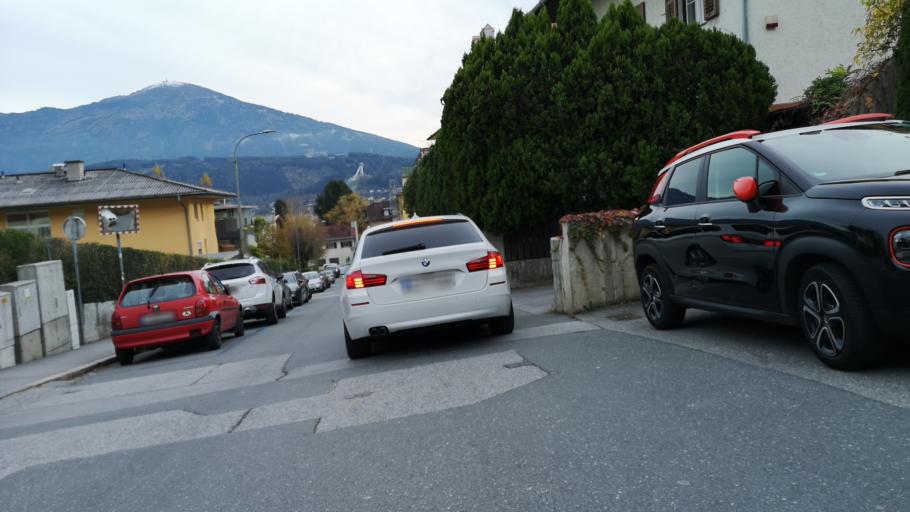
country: AT
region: Tyrol
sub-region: Innsbruck Stadt
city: Innsbruck
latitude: 47.2698
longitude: 11.3820
